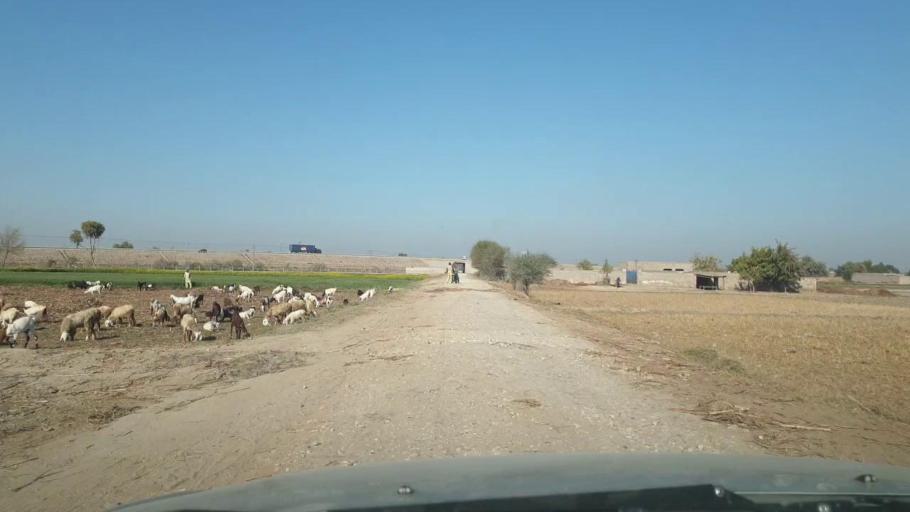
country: PK
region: Sindh
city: Ghotki
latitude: 28.0509
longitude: 69.3376
